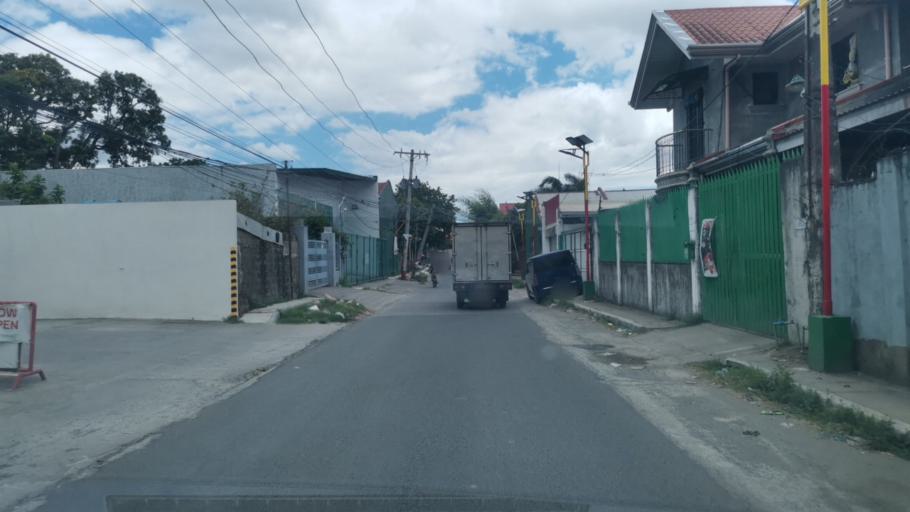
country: PH
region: Calabarzon
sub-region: Province of Batangas
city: Tanauan
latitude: 14.0811
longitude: 121.1443
